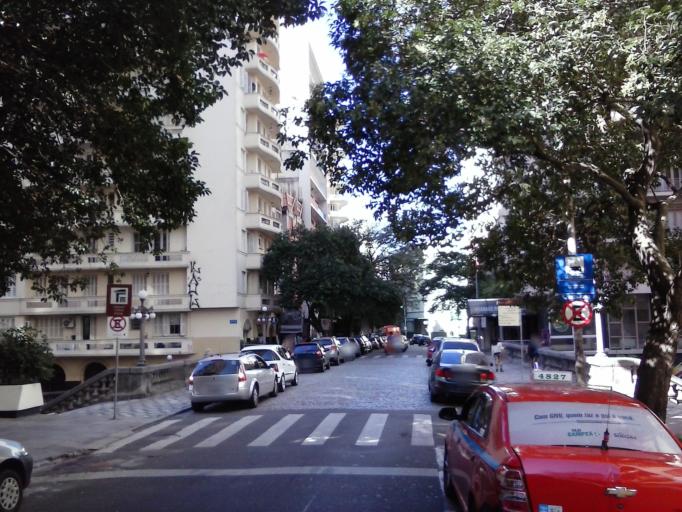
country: BR
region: Rio Grande do Sul
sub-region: Porto Alegre
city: Porto Alegre
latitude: -30.0336
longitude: -51.2281
